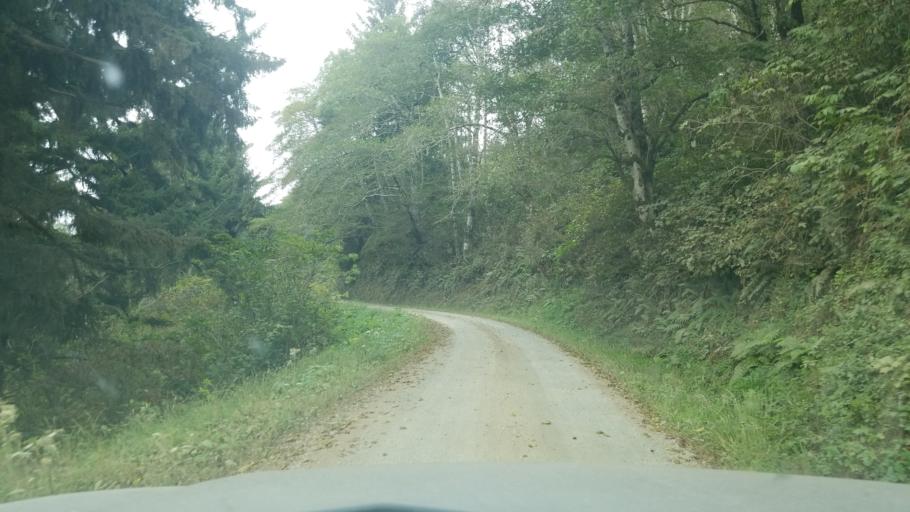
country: US
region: California
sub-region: Del Norte County
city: Bertsch-Oceanview
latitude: 41.5246
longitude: -124.0796
